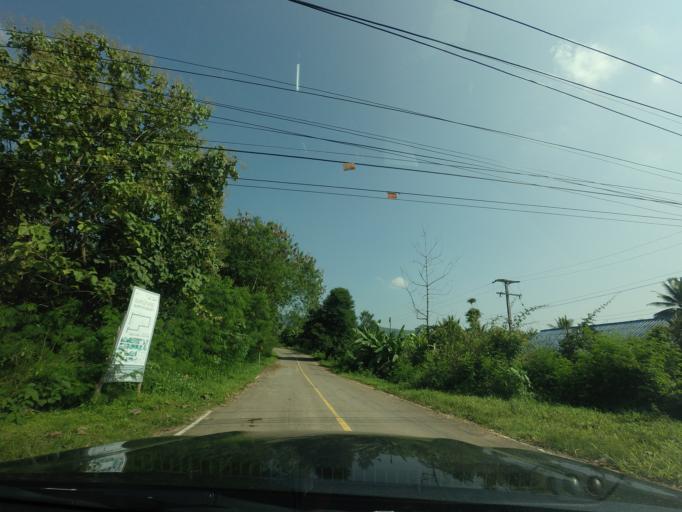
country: TH
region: Loei
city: Na Haeo
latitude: 17.4978
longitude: 101.0170
